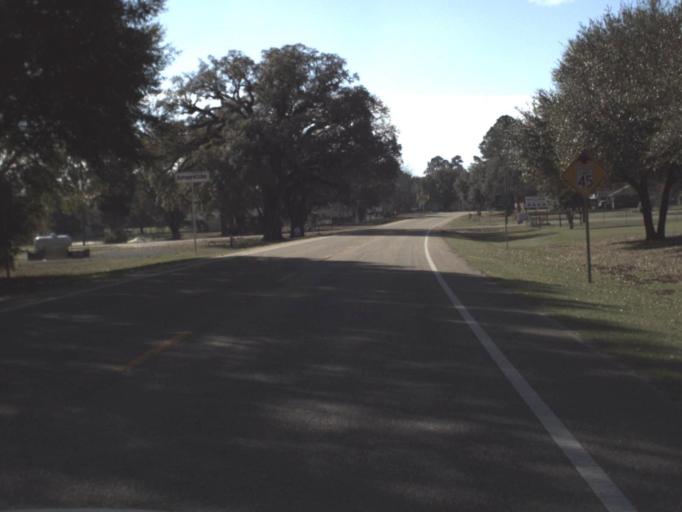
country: US
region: Florida
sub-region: Jackson County
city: Malone
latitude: 30.9655
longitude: -85.1621
